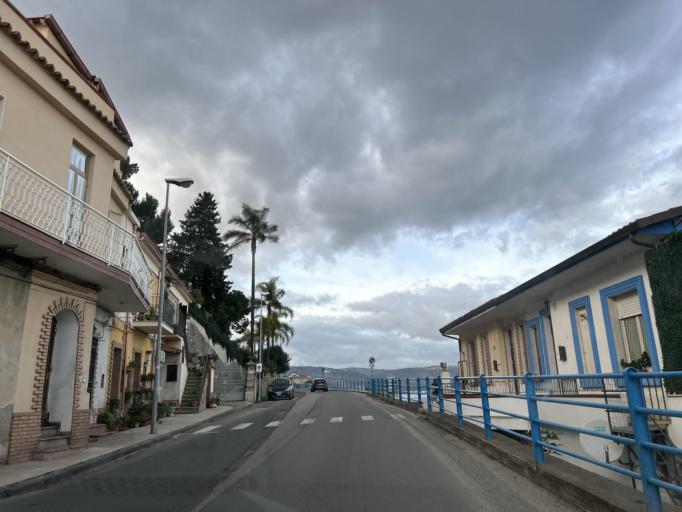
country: IT
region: Calabria
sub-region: Provincia di Catanzaro
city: Soverato Marina
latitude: 38.6923
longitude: 16.5456
